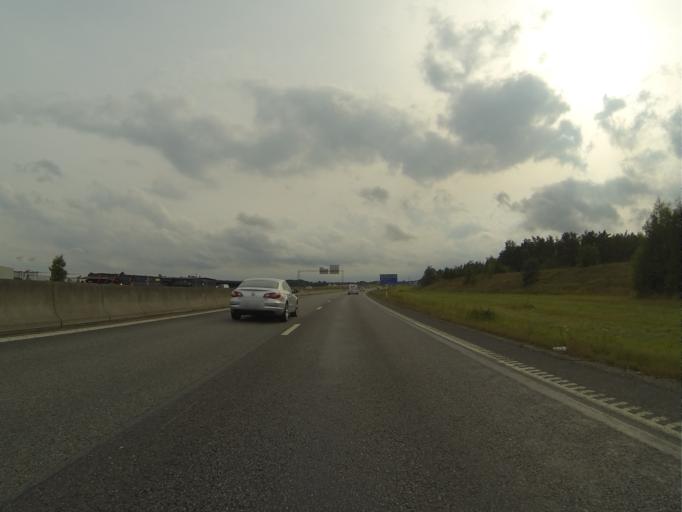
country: SE
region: Skane
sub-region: Kristianstads Kommun
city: Kristianstad
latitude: 56.0141
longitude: 14.1148
